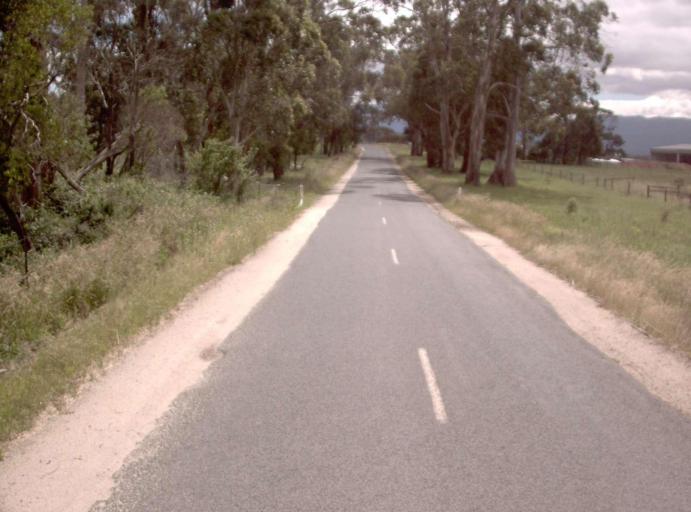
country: AU
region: Victoria
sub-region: Latrobe
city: Moe
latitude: -37.9992
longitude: 146.1449
